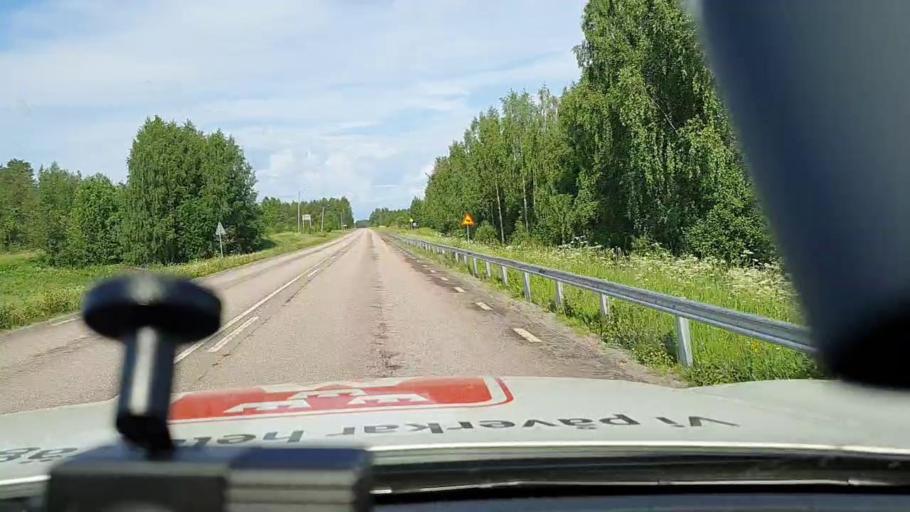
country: SE
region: Norrbotten
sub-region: Alvsbyns Kommun
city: AElvsbyn
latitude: 66.0155
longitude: 21.1600
